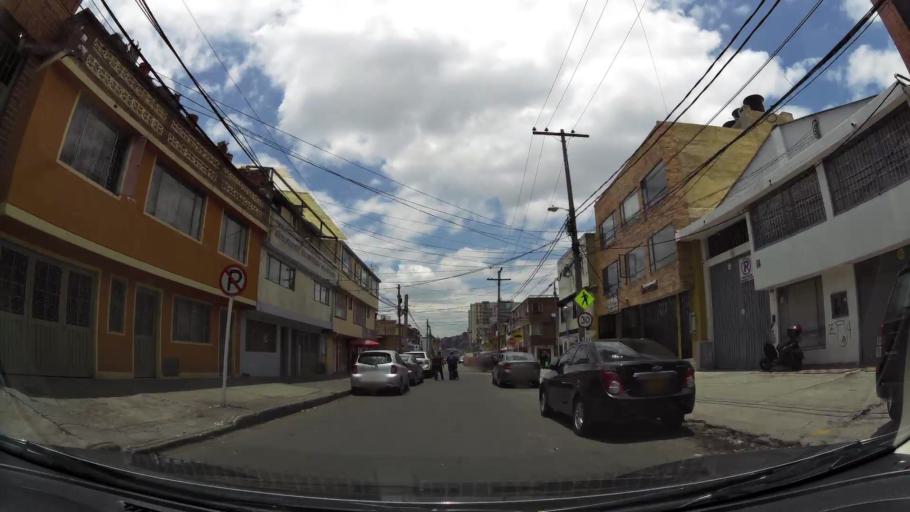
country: CO
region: Bogota D.C.
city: Barrio San Luis
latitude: 4.7138
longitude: -74.0601
